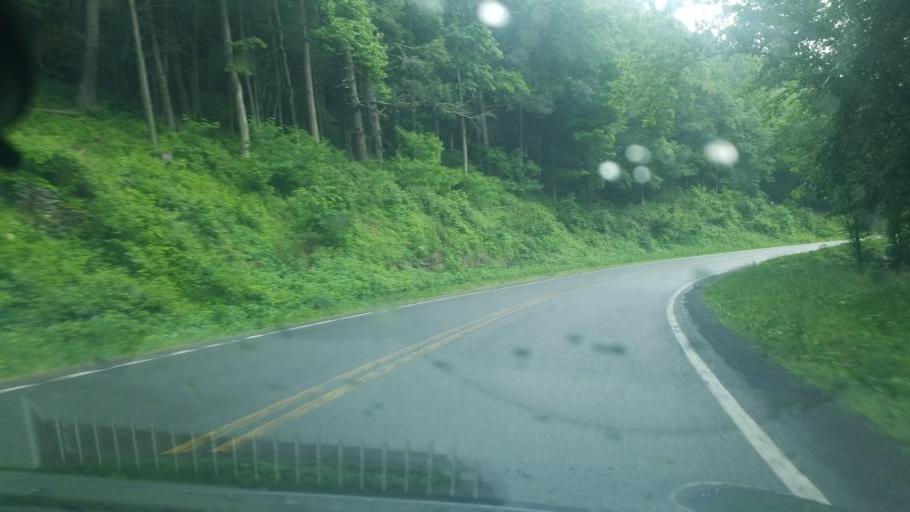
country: US
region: West Virginia
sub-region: Pendleton County
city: Franklin
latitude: 38.6677
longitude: -79.2957
